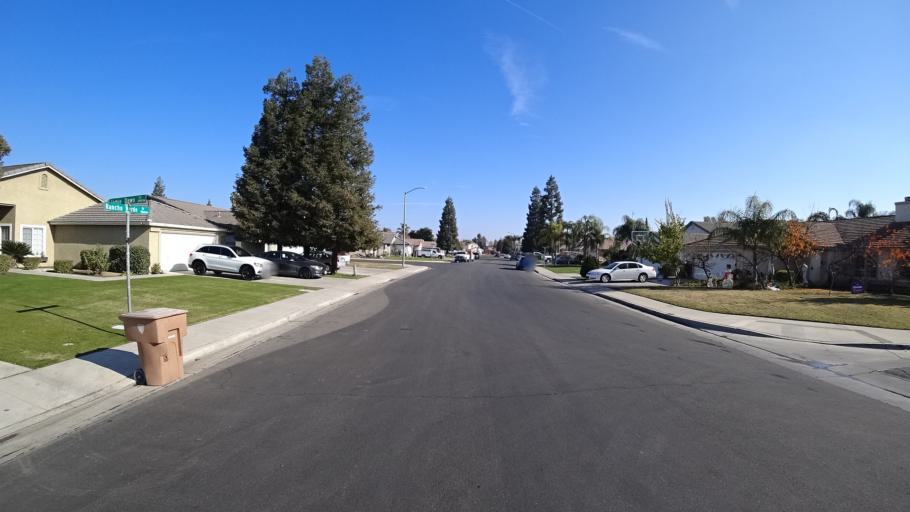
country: US
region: California
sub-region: Kern County
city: Greenacres
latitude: 35.3200
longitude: -119.1126
